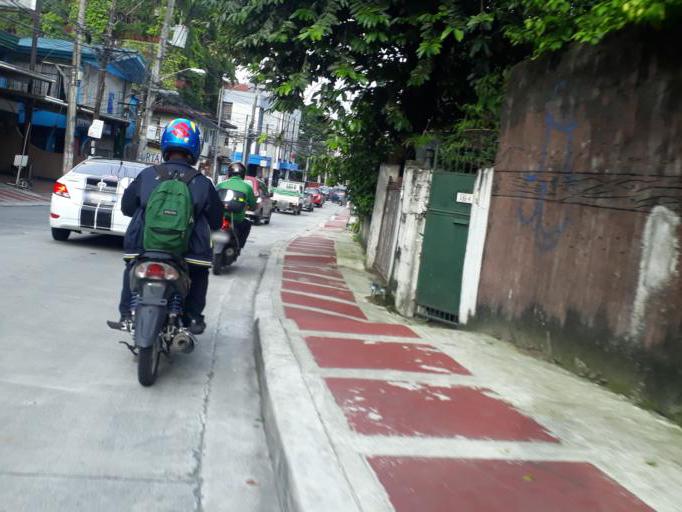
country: PH
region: Metro Manila
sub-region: Quezon City
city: Quezon City
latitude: 14.6354
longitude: 121.0633
